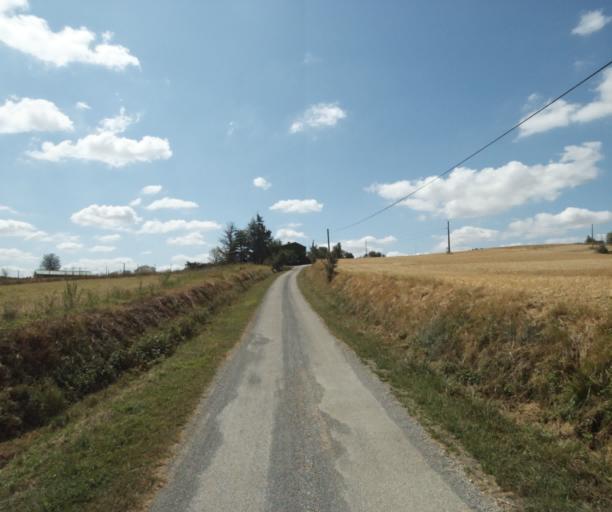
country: FR
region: Midi-Pyrenees
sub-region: Departement de la Haute-Garonne
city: Auriac-sur-Vendinelle
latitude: 43.4795
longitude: 1.8452
